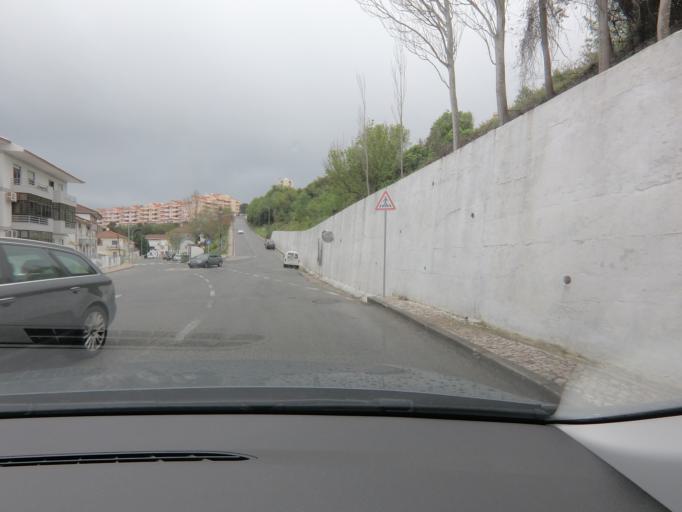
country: PT
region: Lisbon
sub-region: Alenquer
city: Alenquer
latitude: 39.0498
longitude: -9.0078
